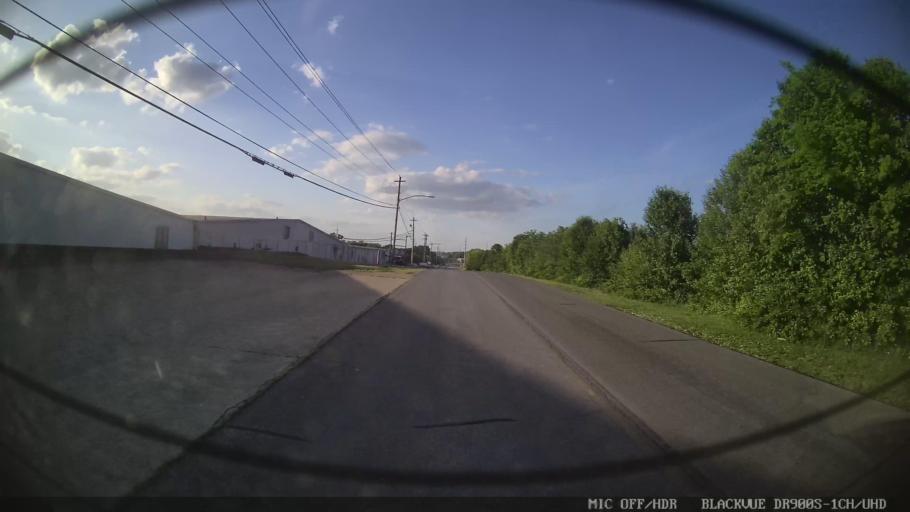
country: US
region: Georgia
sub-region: Bartow County
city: Cartersville
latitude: 34.1485
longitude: -84.7936
